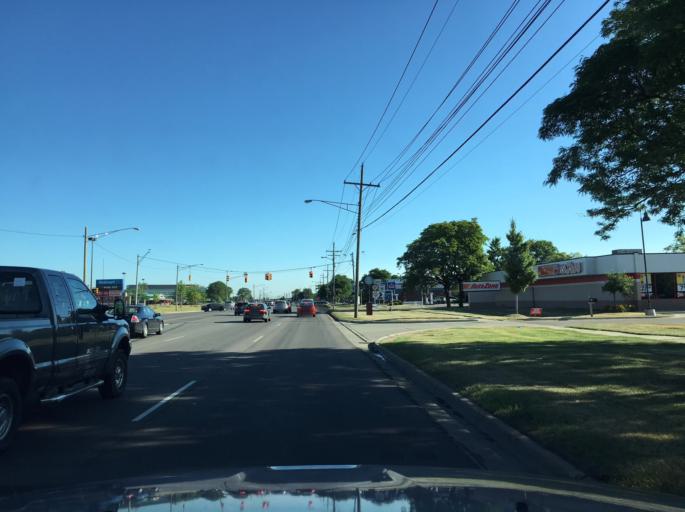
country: US
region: Michigan
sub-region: Macomb County
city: Sterling Heights
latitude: 42.5404
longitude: -83.0289
